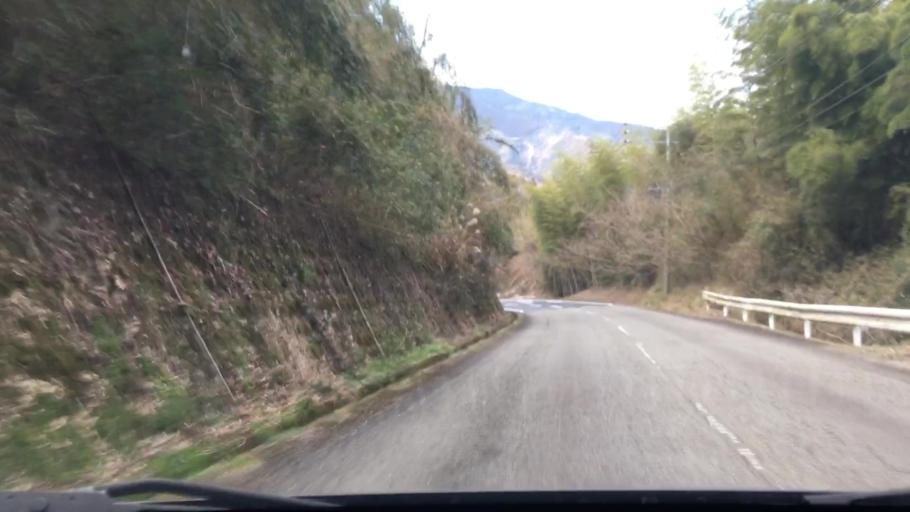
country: JP
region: Miyazaki
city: Nichinan
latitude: 31.7051
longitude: 131.3305
